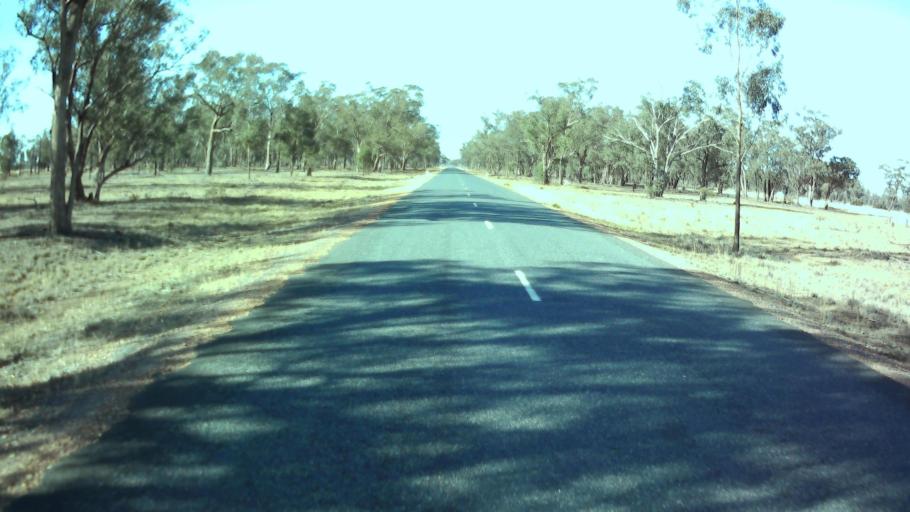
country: AU
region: New South Wales
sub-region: Weddin
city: Grenfell
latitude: -34.0616
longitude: 147.9094
